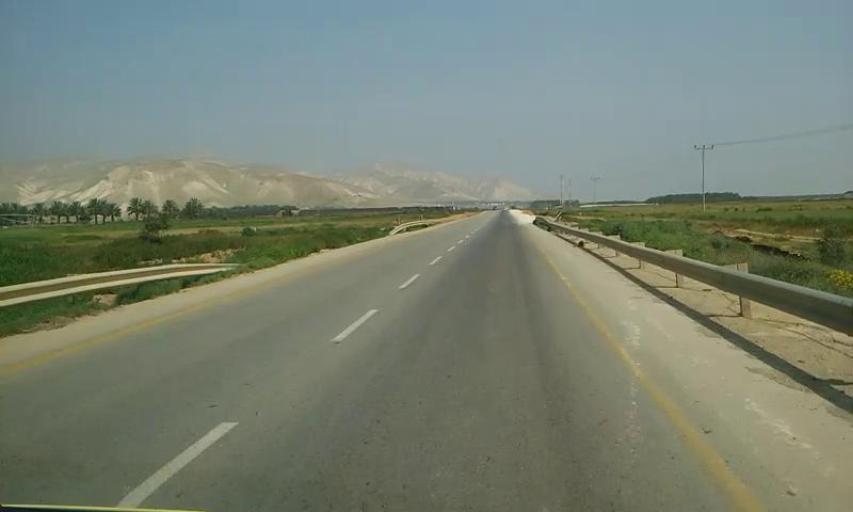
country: PS
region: West Bank
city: Al Fasayil
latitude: 32.0347
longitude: 35.4550
